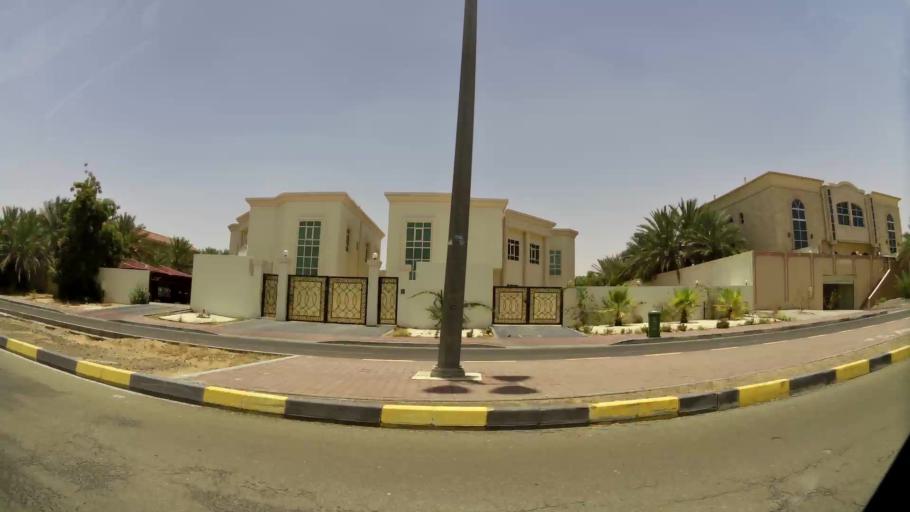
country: OM
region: Al Buraimi
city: Al Buraymi
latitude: 24.2636
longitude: 55.7308
